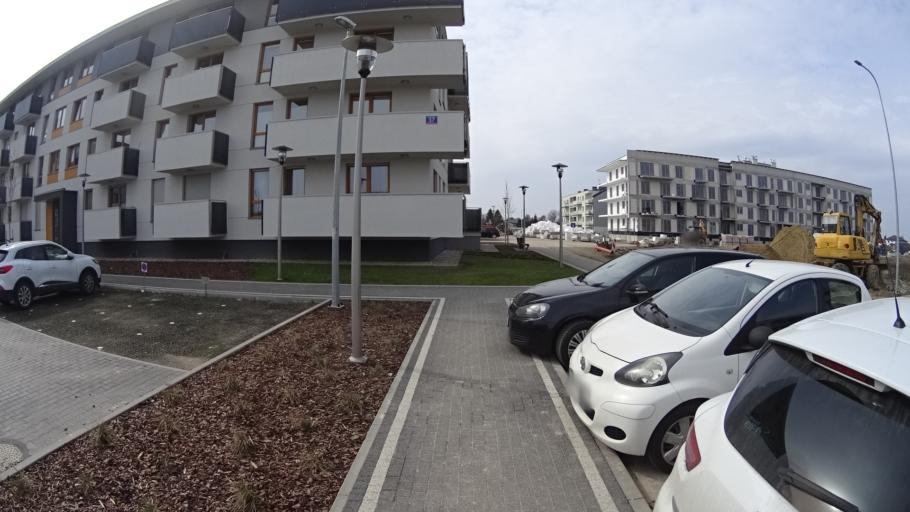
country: PL
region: Masovian Voivodeship
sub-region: Powiat warszawski zachodni
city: Ozarow Mazowiecki
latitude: 52.2180
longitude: 20.7907
